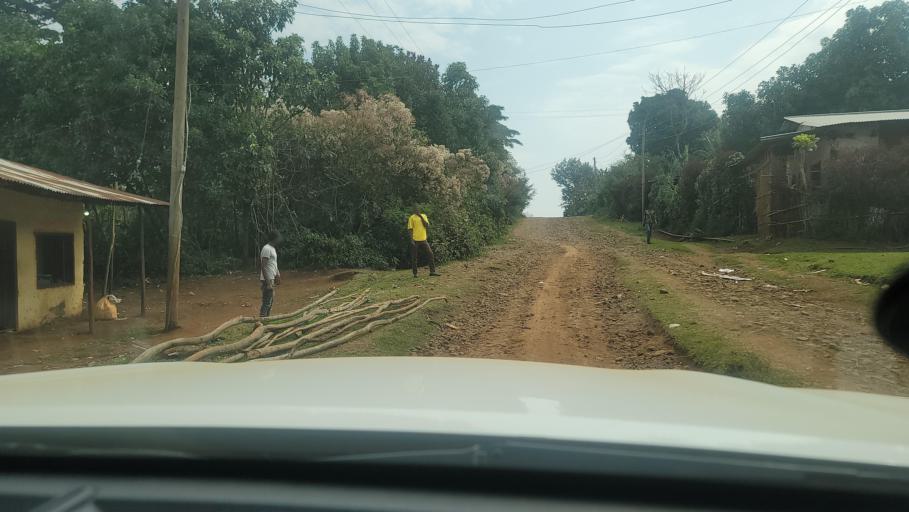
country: ET
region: Oromiya
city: Agaro
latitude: 7.8091
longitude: 36.4703
